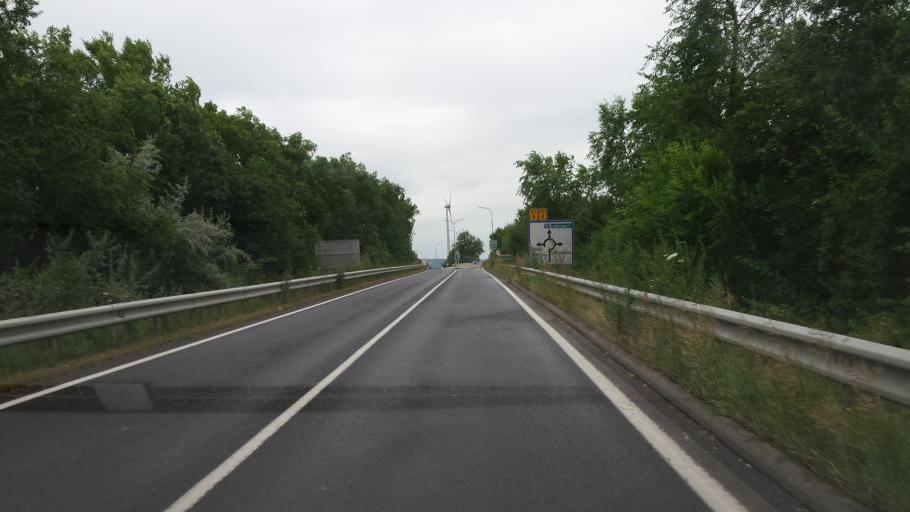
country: AT
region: Lower Austria
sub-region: Politischer Bezirk Bruck an der Leitha
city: Bruck an der Leitha
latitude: 48.0420
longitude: 16.7539
